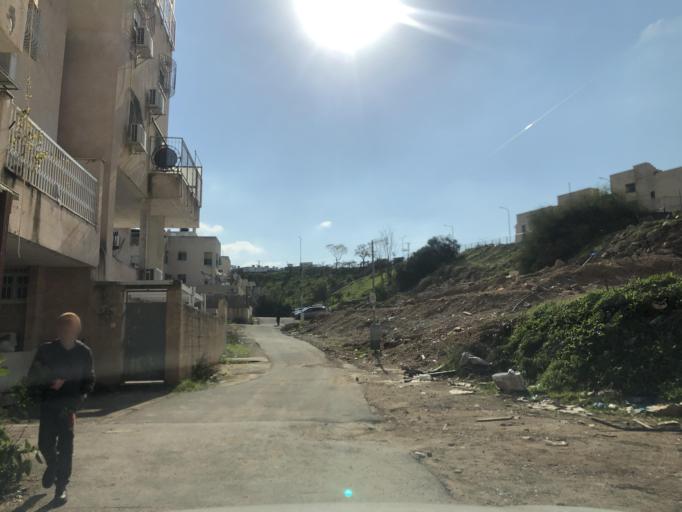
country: IL
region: Jerusalem
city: Modiin Ilit
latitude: 31.9336
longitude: 35.0390
